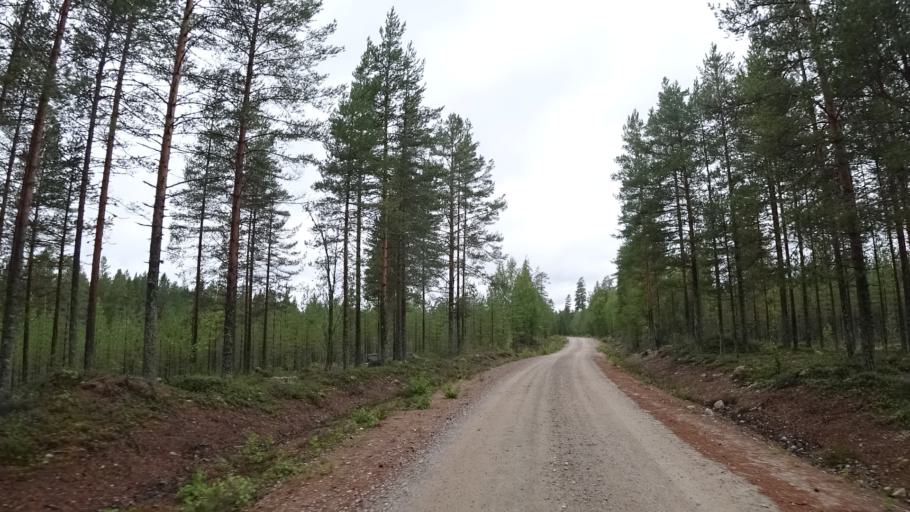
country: FI
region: North Karelia
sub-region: Pielisen Karjala
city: Lieksa
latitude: 63.5070
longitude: 30.1452
